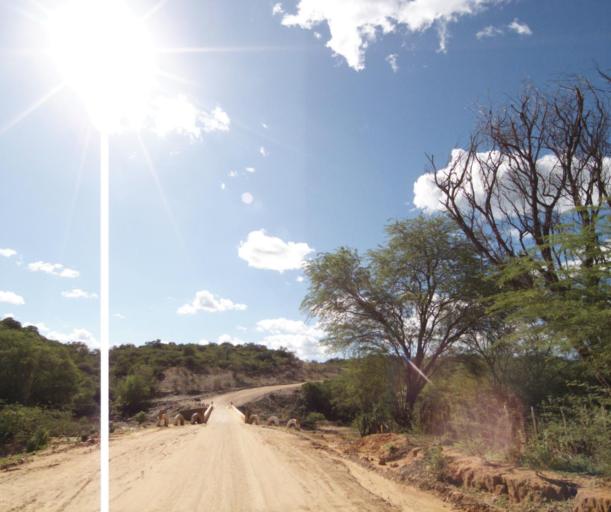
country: BR
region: Bahia
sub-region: Pocoes
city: Pocoes
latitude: -14.2416
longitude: -40.7769
